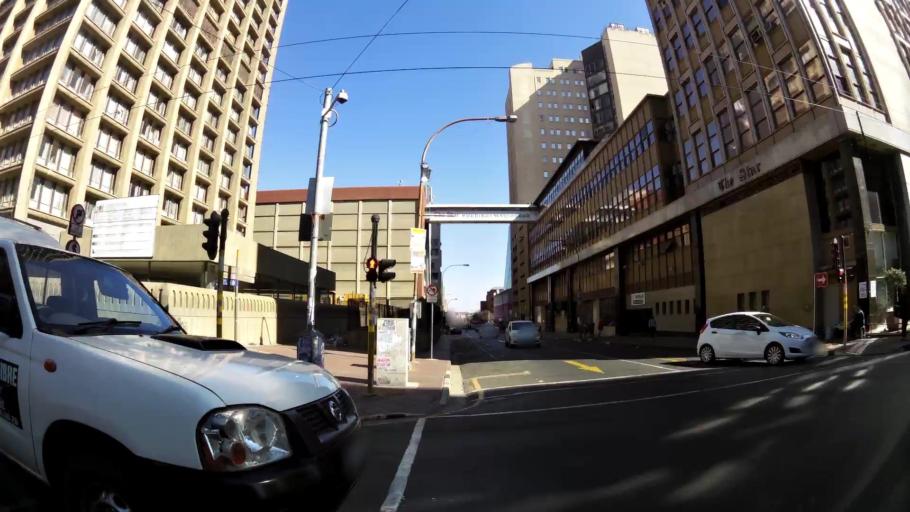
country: ZA
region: Gauteng
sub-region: City of Johannesburg Metropolitan Municipality
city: Johannesburg
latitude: -26.2044
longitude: 28.0379
